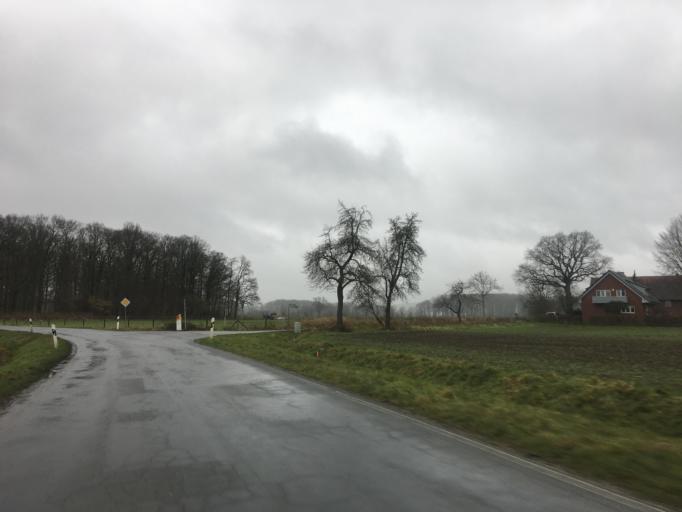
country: DE
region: North Rhine-Westphalia
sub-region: Regierungsbezirk Munster
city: Havixbeck
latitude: 51.9656
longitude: 7.4659
